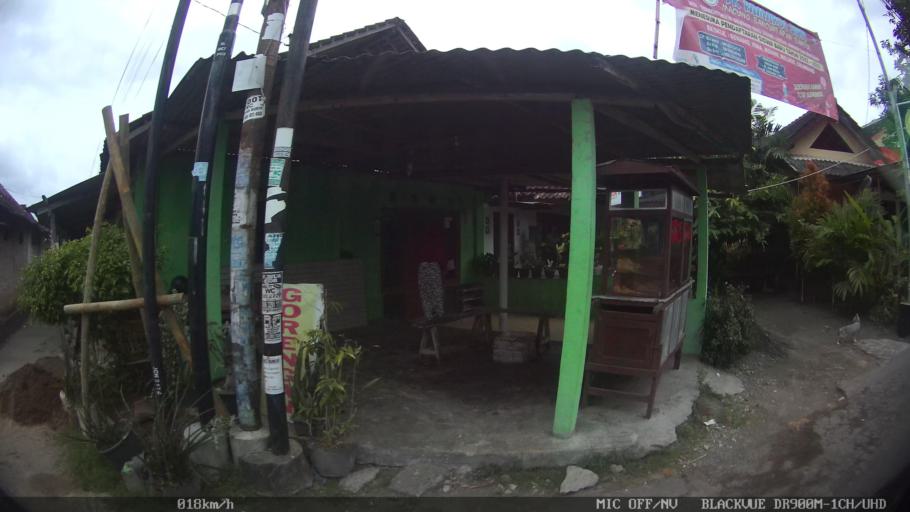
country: ID
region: Daerah Istimewa Yogyakarta
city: Depok
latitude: -7.8064
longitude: 110.4159
